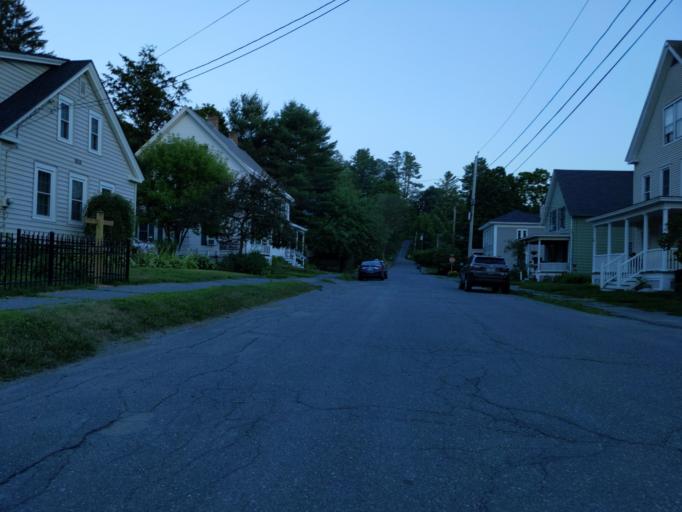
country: US
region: New Hampshire
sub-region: Grafton County
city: Lebanon
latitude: 43.6411
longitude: -72.2463
